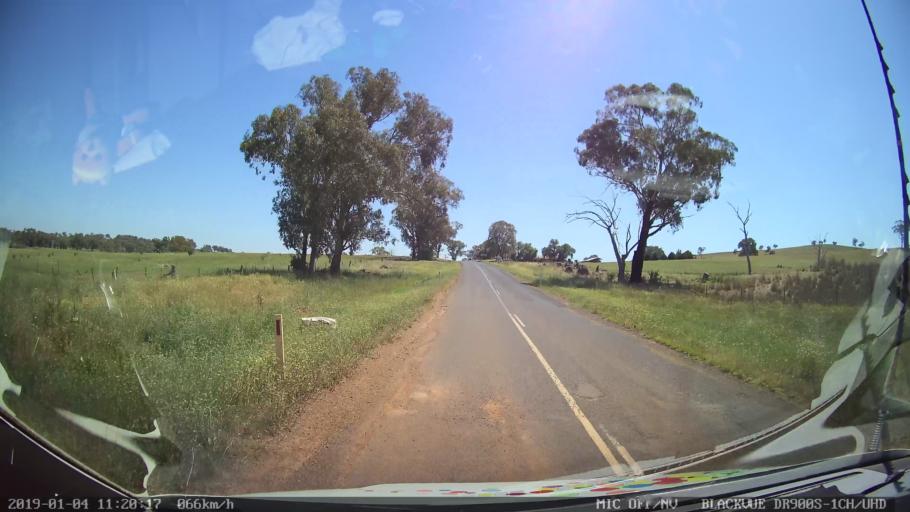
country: AU
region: New South Wales
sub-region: Cabonne
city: Molong
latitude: -33.1652
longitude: 148.7062
